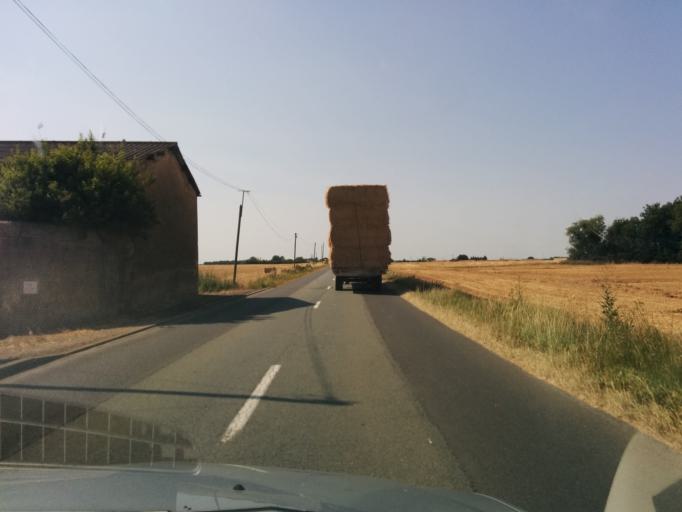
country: FR
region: Poitou-Charentes
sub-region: Departement de la Vienne
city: Mirebeau
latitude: 46.7412
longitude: 0.1825
